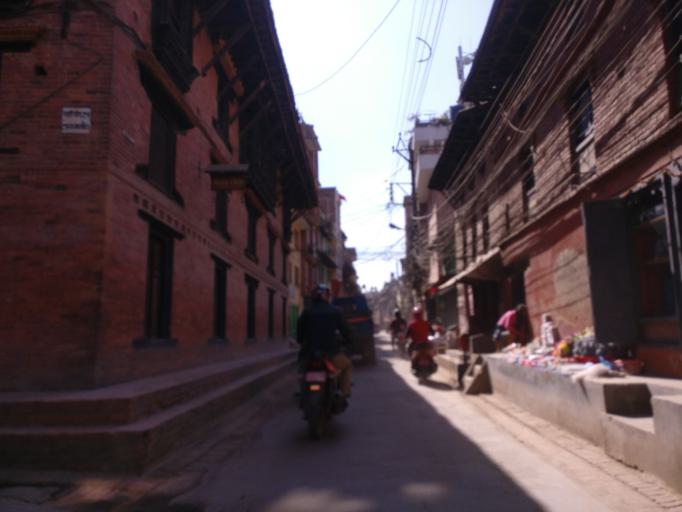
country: NP
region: Central Region
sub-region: Bagmati Zone
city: Patan
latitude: 27.6755
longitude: 85.3262
